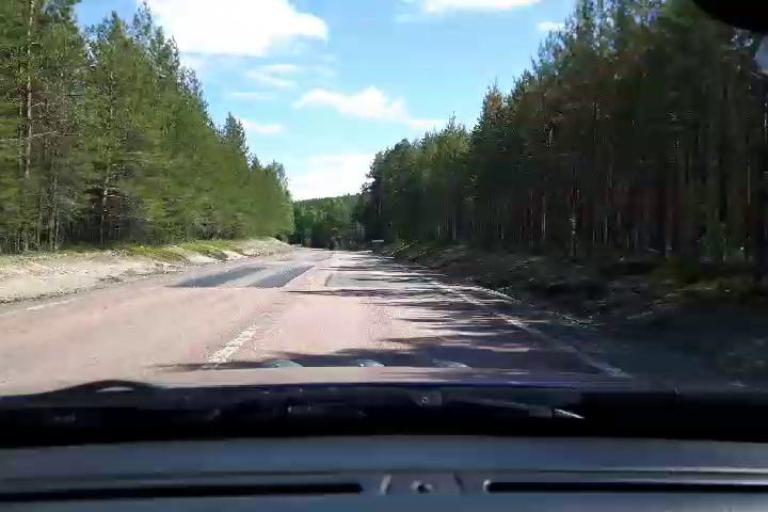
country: SE
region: Gaevleborg
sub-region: Ljusdals Kommun
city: Farila
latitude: 61.8893
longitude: 15.6713
